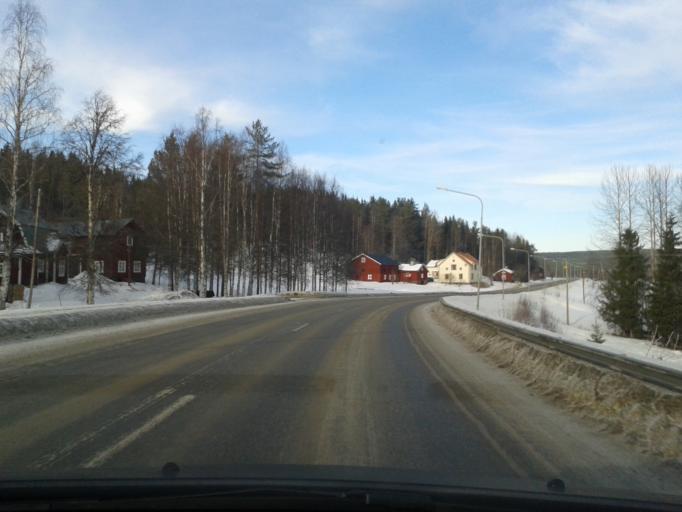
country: SE
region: Vaesternorrland
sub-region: OErnskoeldsviks Kommun
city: Bredbyn
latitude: 63.4925
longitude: 18.0800
